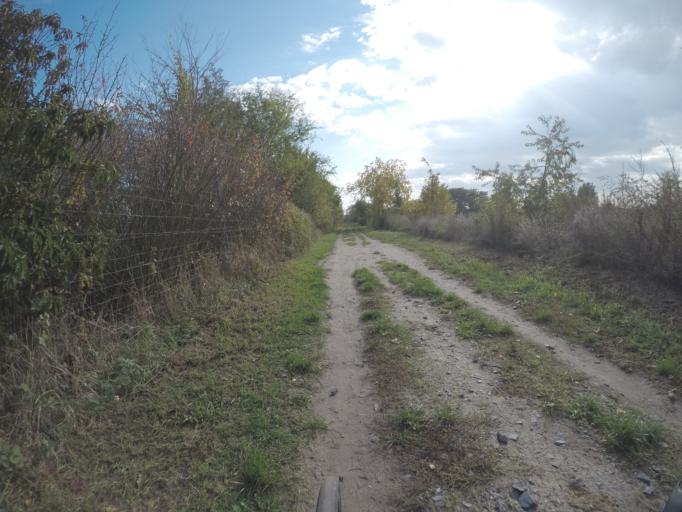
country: DE
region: Brandenburg
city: Hohen Neuendorf
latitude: 52.6499
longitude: 13.2595
